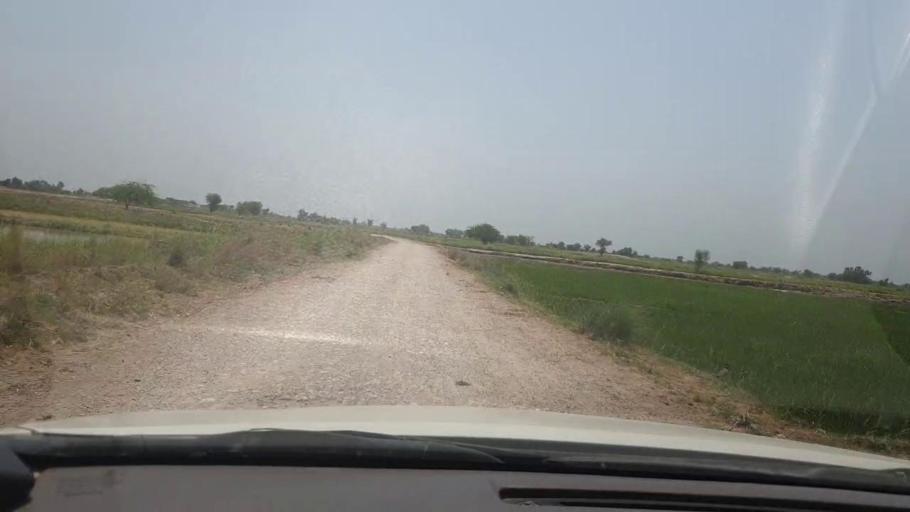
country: PK
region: Sindh
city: Garhi Yasin
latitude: 27.9184
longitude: 68.5545
